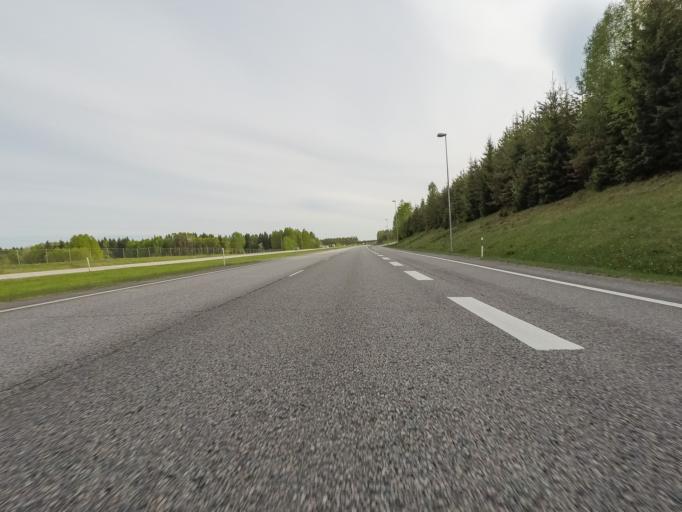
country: FI
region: Uusimaa
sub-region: Helsinki
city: Nurmijaervi
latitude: 60.4619
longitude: 24.8485
